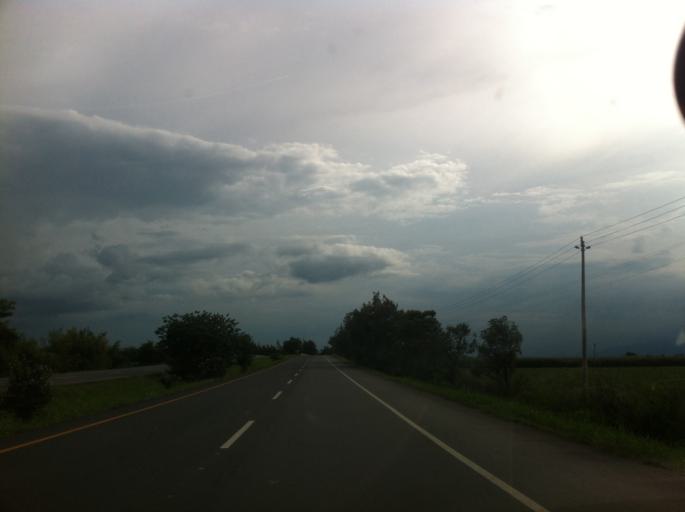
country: CO
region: Valle del Cauca
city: Palmira
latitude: 3.5730
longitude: -76.3302
